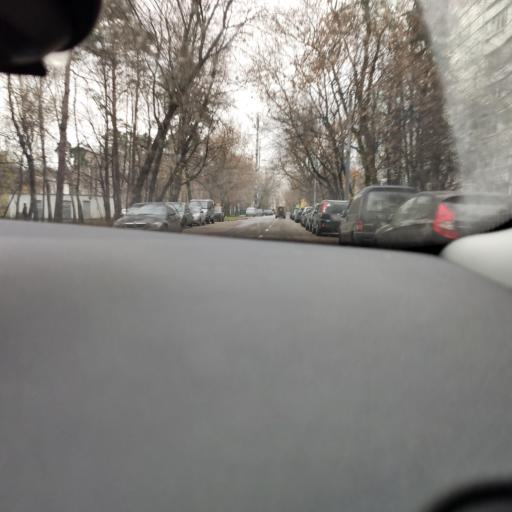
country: RU
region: Moscow
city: Vatutino
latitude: 55.8862
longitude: 37.6962
